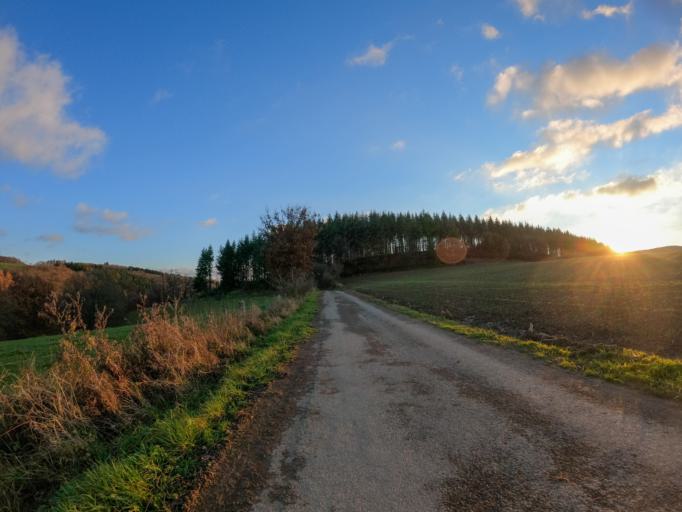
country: LU
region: Diekirch
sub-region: Canton de Wiltz
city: Bavigne
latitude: 49.9233
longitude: 5.8547
